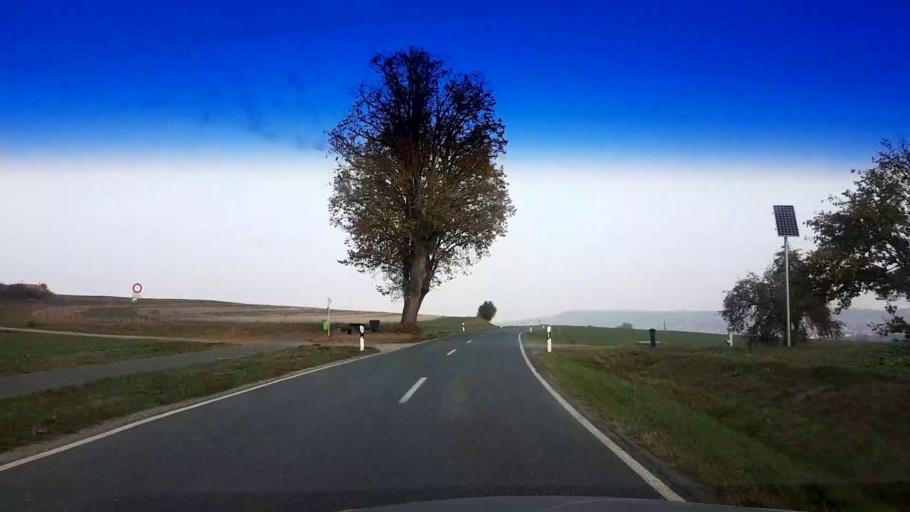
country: DE
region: Bavaria
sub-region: Upper Franconia
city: Altenkunstadt
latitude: 50.1140
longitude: 11.2522
